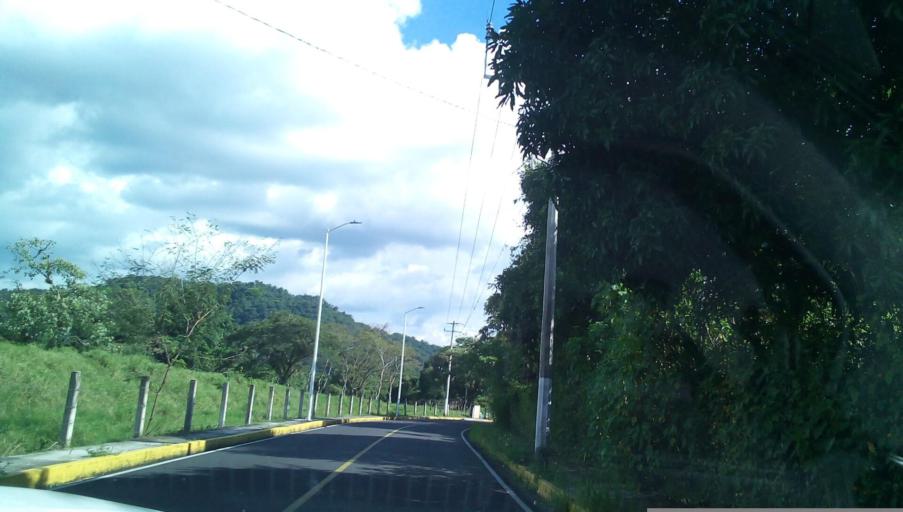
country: MX
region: Veracruz
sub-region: Cordoba
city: El Porvenir
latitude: 18.9056
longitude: -96.9235
